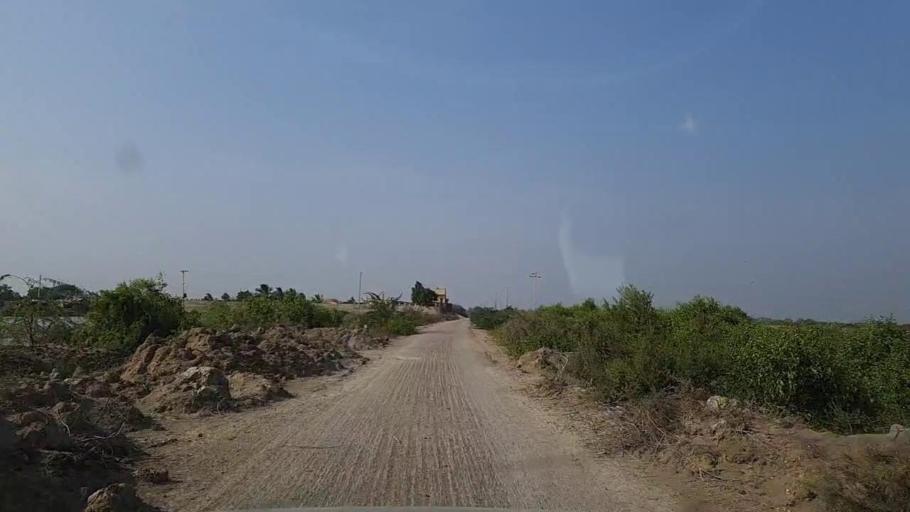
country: PK
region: Sindh
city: Mirpur Sakro
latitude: 24.5739
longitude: 67.5714
